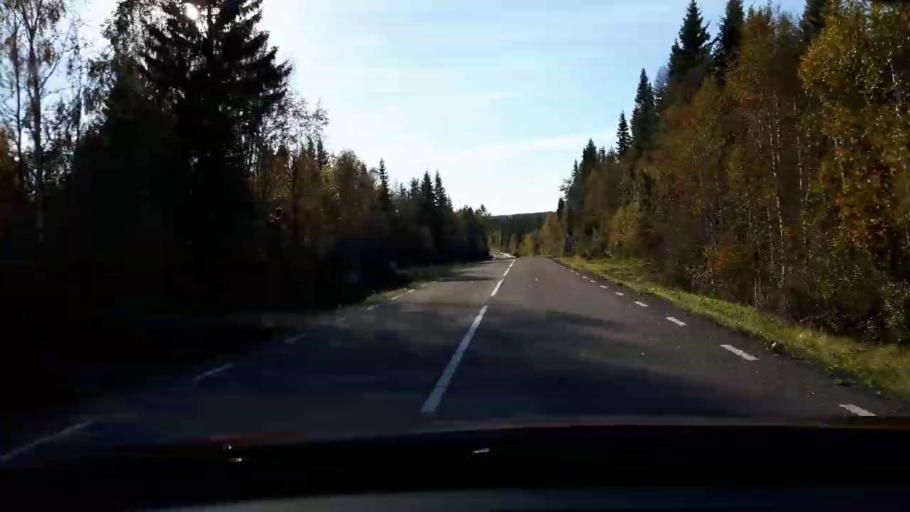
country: SE
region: Jaemtland
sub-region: Stroemsunds Kommun
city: Stroemsund
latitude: 63.8670
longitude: 15.1105
